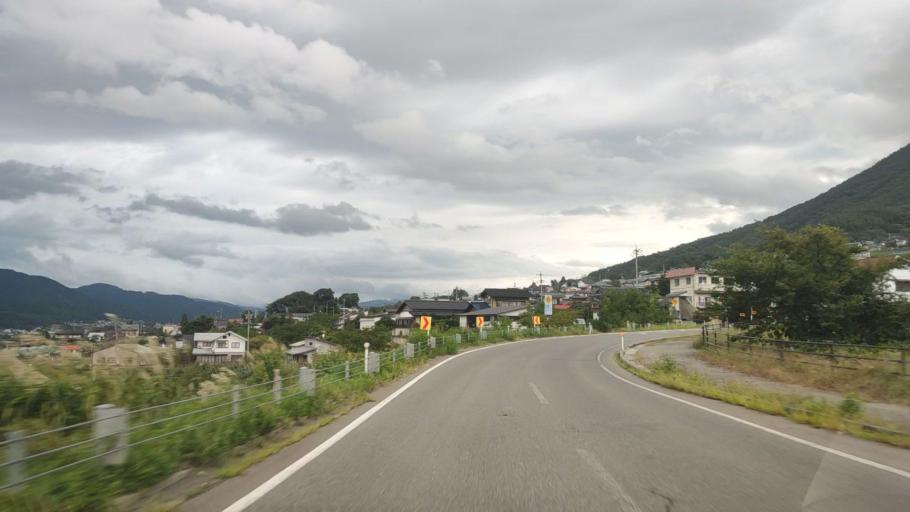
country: JP
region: Nagano
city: Nakano
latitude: 36.7957
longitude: 138.3611
